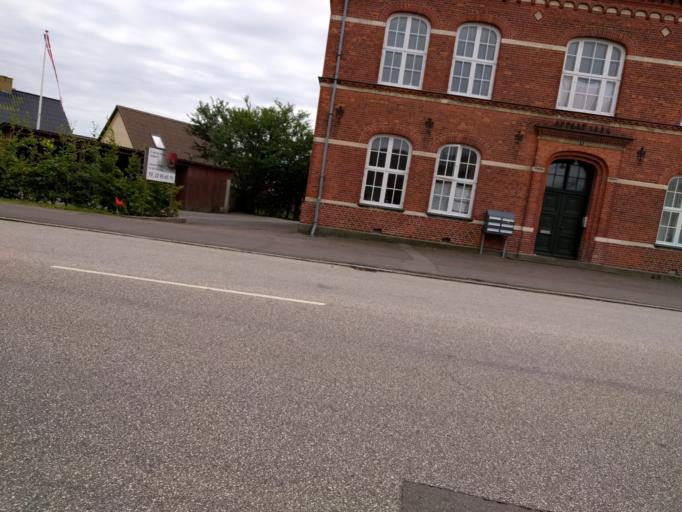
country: DK
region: Zealand
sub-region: Guldborgsund Kommune
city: Stubbekobing
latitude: 54.8882
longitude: 12.0405
